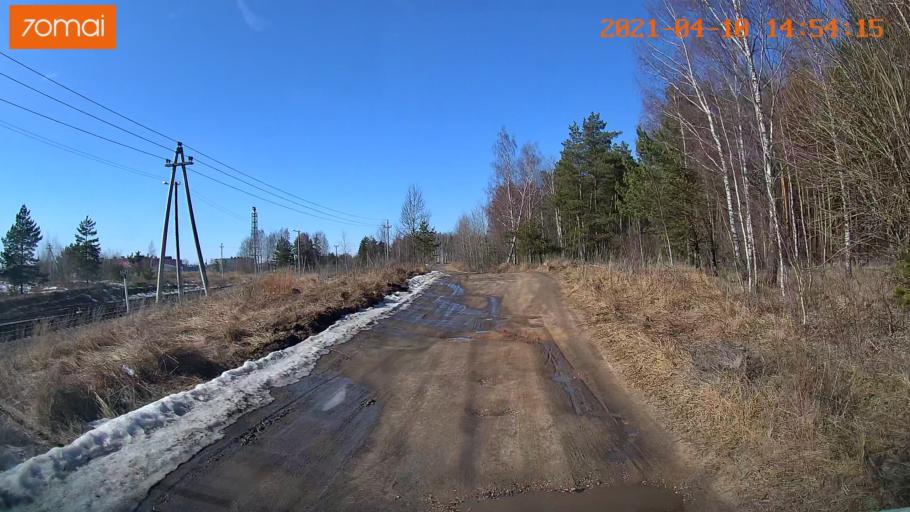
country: RU
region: Ivanovo
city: Kokhma
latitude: 56.9875
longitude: 41.0588
